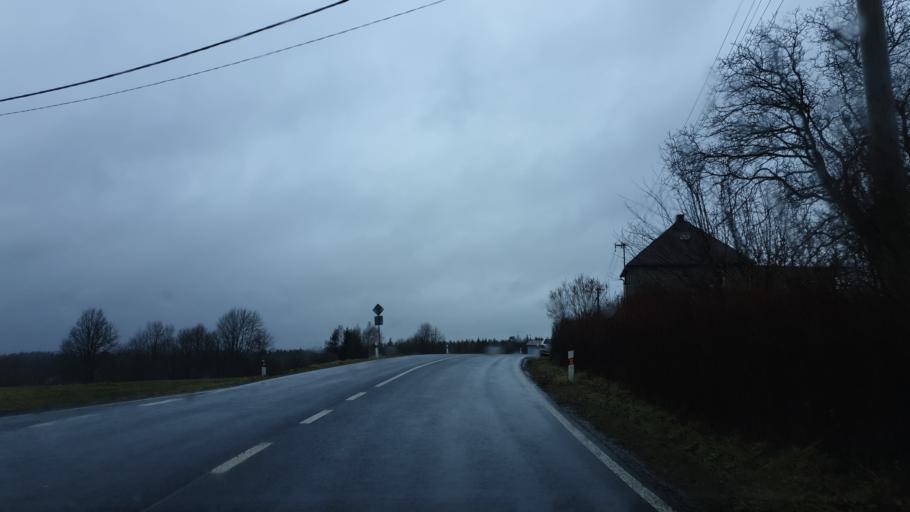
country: CZ
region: Karlovarsky
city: Hranice
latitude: 50.2764
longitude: 12.1857
